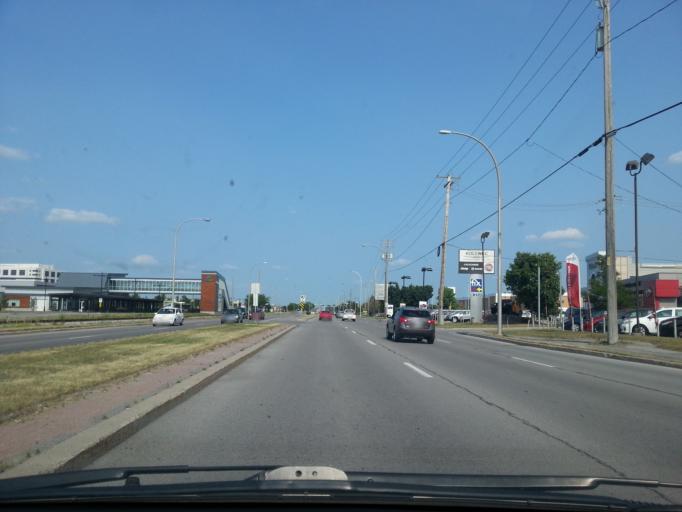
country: CA
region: Quebec
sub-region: Outaouais
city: Gatineau
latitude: 45.4803
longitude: -75.6855
